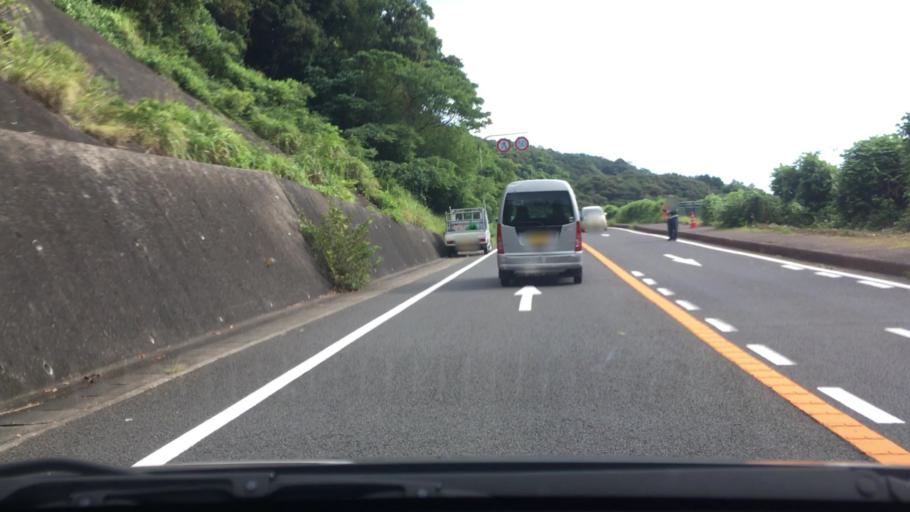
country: JP
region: Nagasaki
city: Togitsu
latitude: 32.8419
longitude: 129.7060
